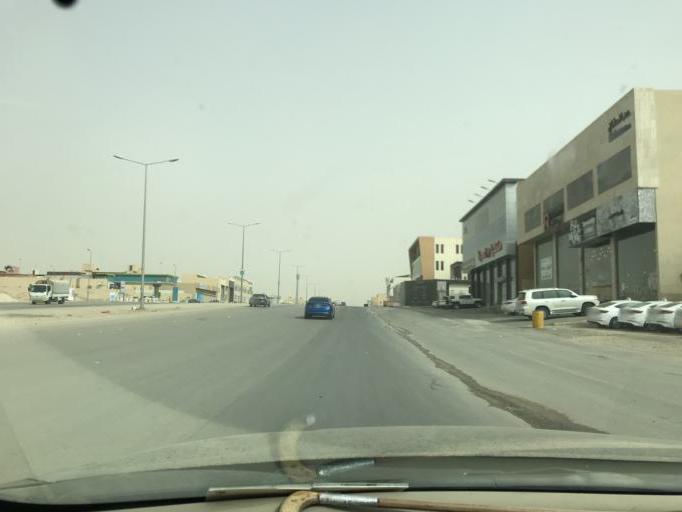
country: SA
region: Ar Riyad
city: Riyadh
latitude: 24.8162
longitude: 46.5978
